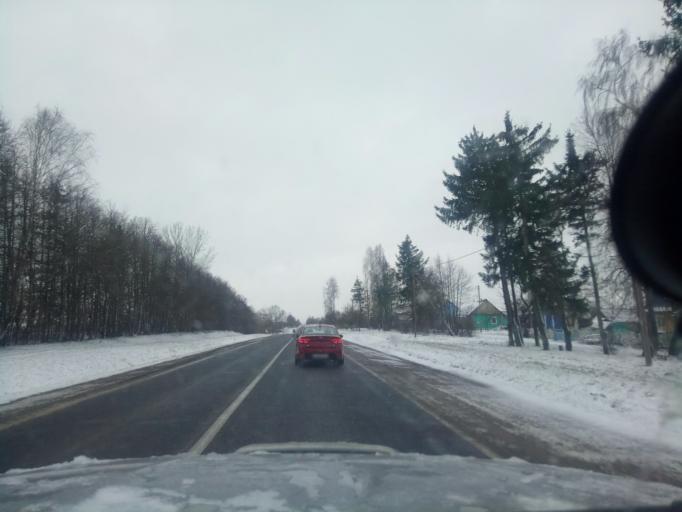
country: BY
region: Minsk
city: Klyetsk
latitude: 53.1339
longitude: 26.6740
